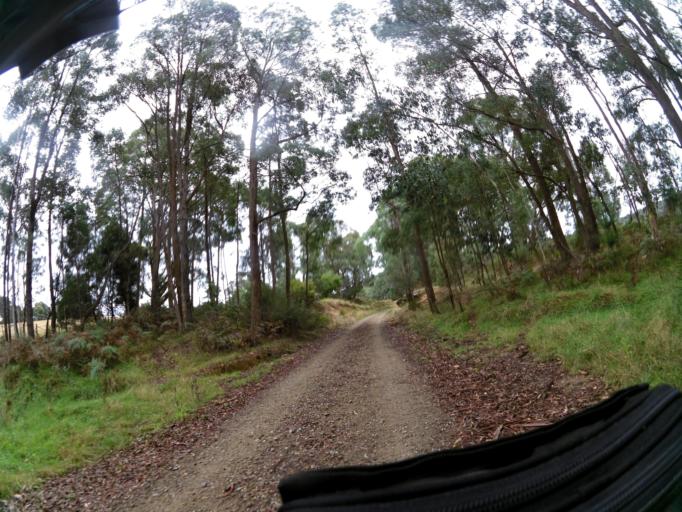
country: AU
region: New South Wales
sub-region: Greater Hume Shire
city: Holbrook
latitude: -36.1501
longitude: 147.4727
